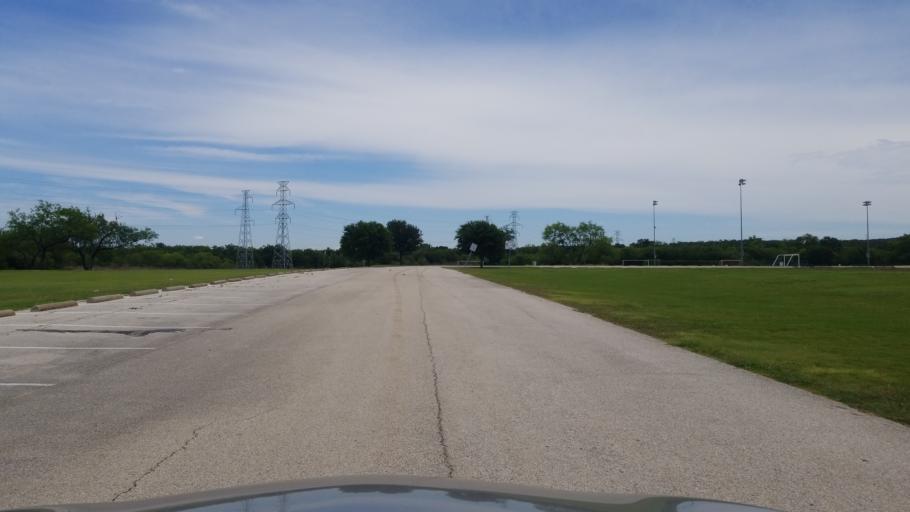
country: US
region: Texas
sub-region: Dallas County
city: Grand Prairie
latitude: 32.6861
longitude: -96.9835
